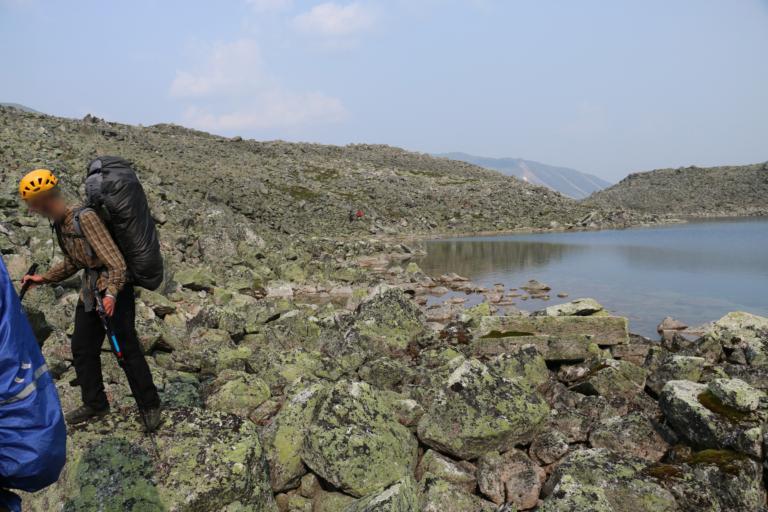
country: RU
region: Respublika Buryatiya
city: Novyy Uoyan
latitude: 56.2136
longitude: 111.0167
